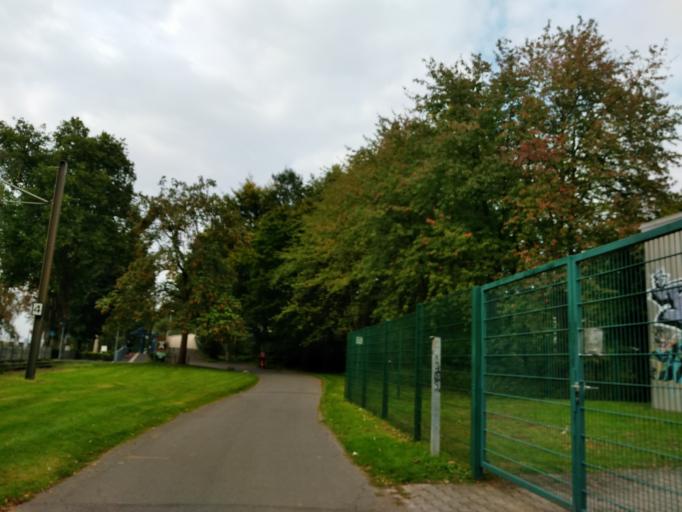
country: DE
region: North Rhine-Westphalia
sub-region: Regierungsbezirk Koln
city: Bad Honnef
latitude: 50.6480
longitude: 7.2155
